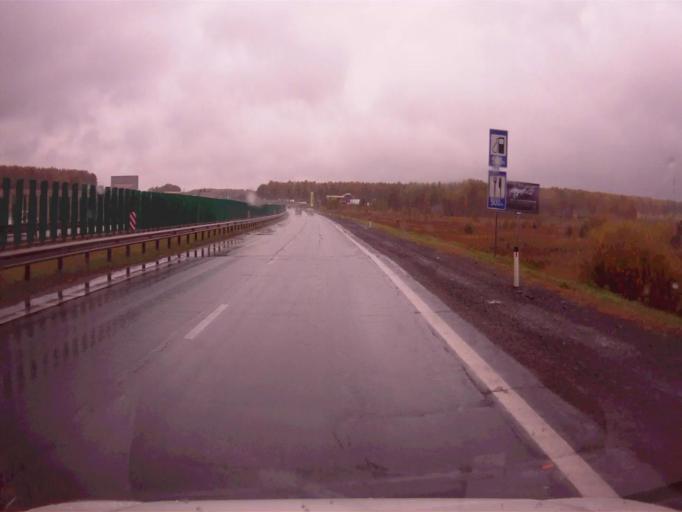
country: RU
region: Chelyabinsk
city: Dolgoderevenskoye
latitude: 55.3224
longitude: 61.3328
